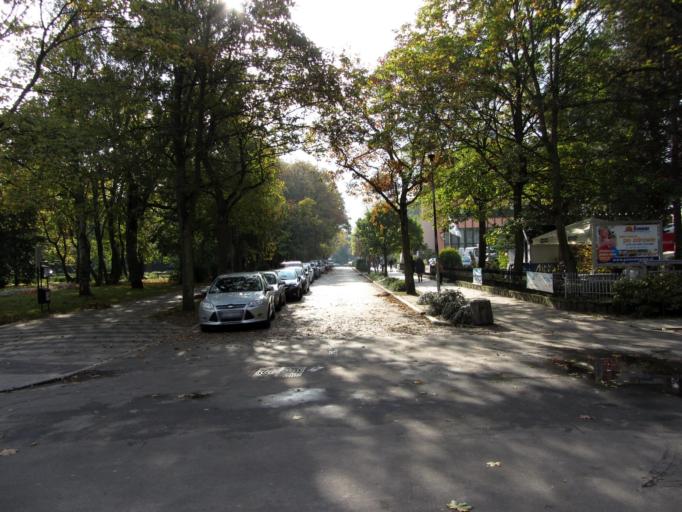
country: PL
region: West Pomeranian Voivodeship
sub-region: Powiat kolobrzeski
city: Kolobrzeg
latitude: 54.1846
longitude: 15.5756
